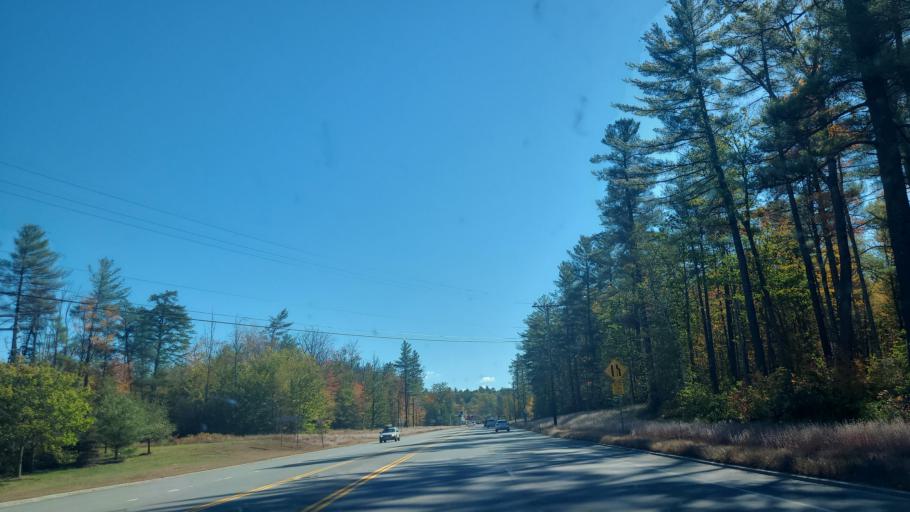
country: US
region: New Hampshire
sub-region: Carroll County
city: Conway
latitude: 44.0158
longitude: -71.1070
